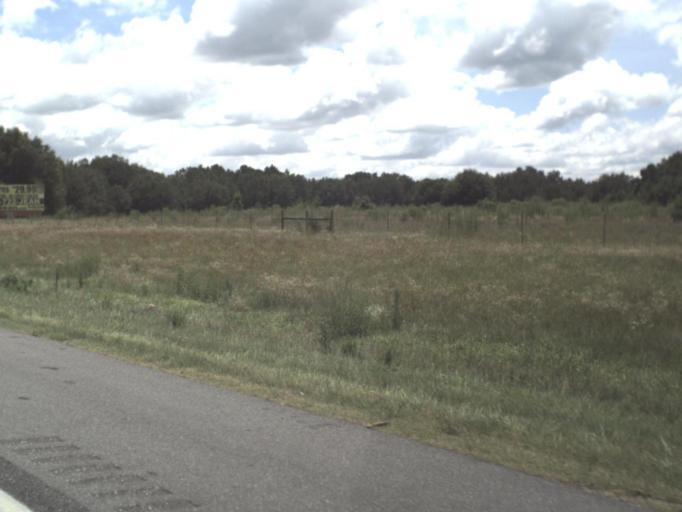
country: US
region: Florida
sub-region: Alachua County
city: High Springs
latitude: 29.9966
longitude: -82.5905
